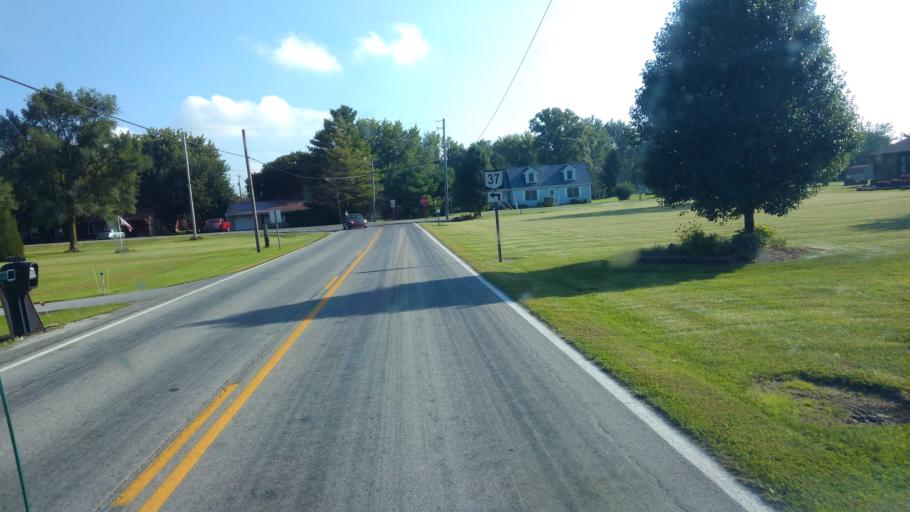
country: US
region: Ohio
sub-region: Hardin County
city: Forest
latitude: 40.8045
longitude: -83.5202
